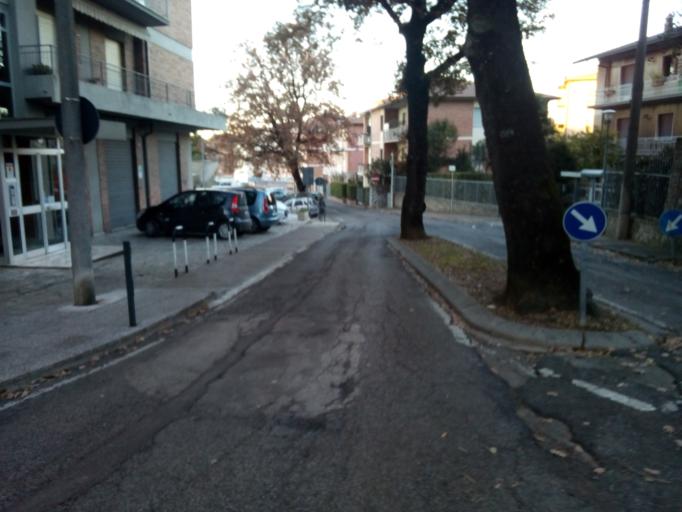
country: IT
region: Umbria
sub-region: Provincia di Perugia
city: Perugia
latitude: 43.0954
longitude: 12.3891
